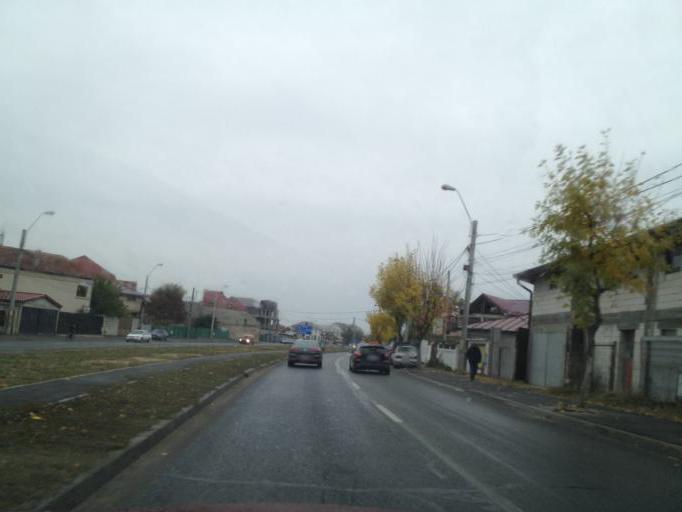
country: RO
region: Dolj
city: Craiova
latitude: 44.3144
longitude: 23.7781
